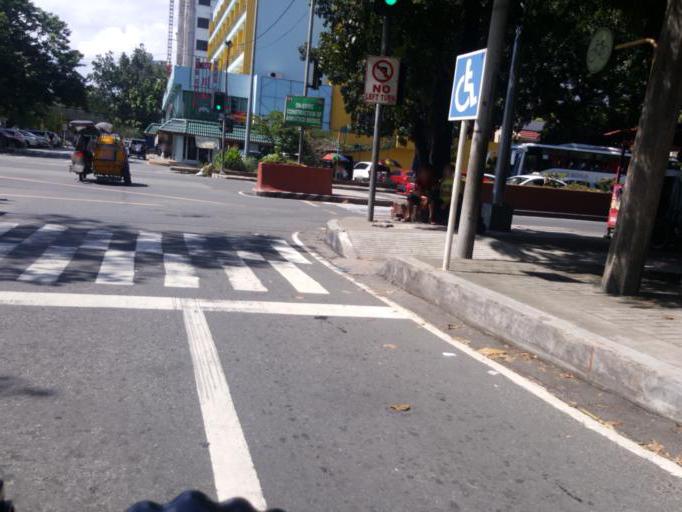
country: PH
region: Metro Manila
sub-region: City of Manila
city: Port Area
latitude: 14.5641
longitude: 120.9855
